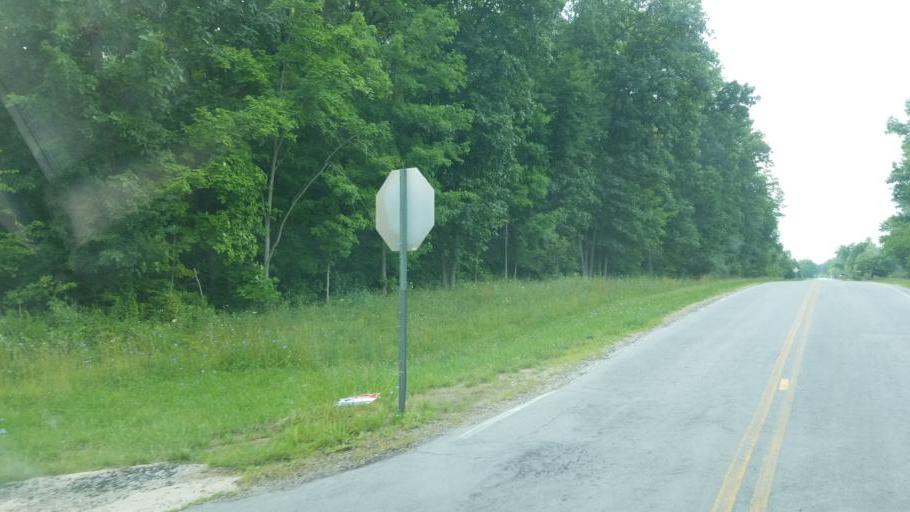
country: US
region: Ohio
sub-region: Union County
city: New California
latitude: 40.1756
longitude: -83.1590
